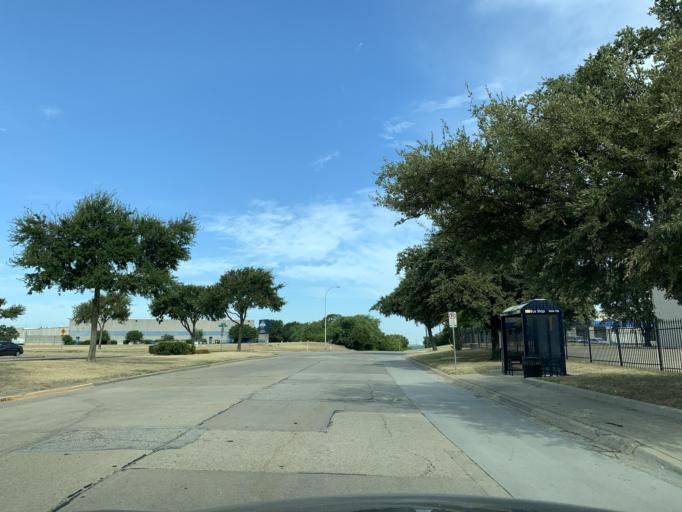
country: US
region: Texas
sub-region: Dallas County
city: Cockrell Hill
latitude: 32.7703
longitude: -96.8681
